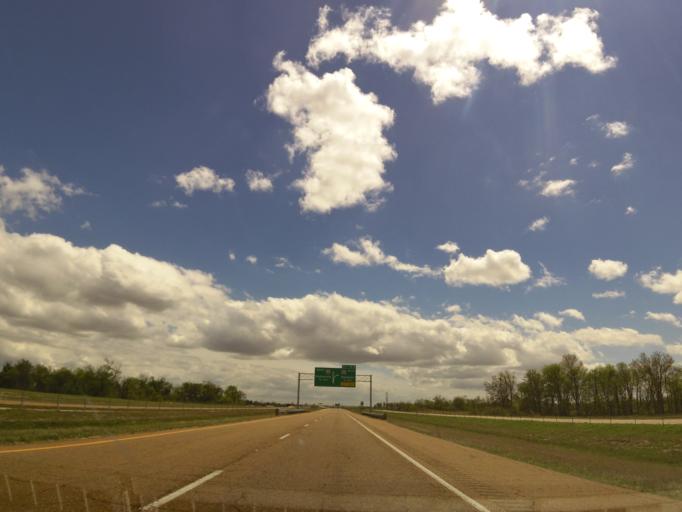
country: US
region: Arkansas
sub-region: Poinsett County
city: Marked Tree
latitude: 35.4055
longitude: -90.2800
